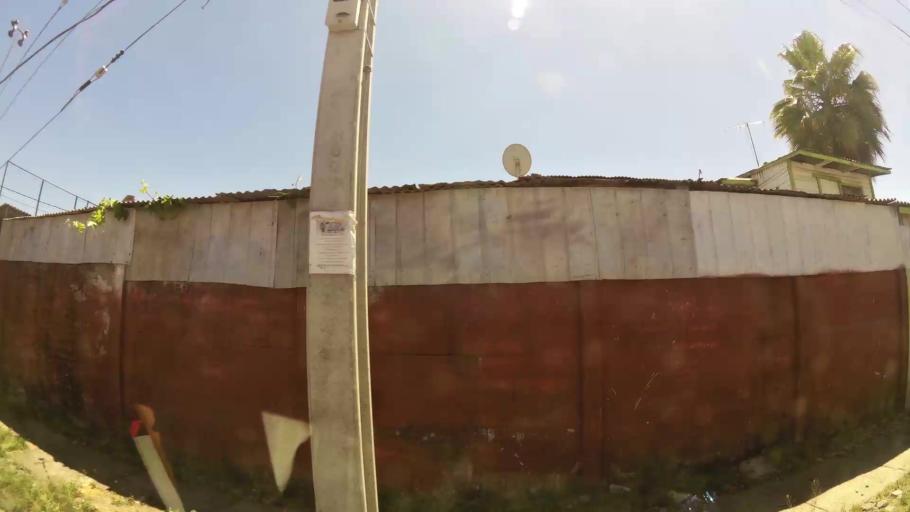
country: CL
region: Santiago Metropolitan
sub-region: Provincia de Santiago
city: La Pintana
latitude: -33.5714
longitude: -70.6663
